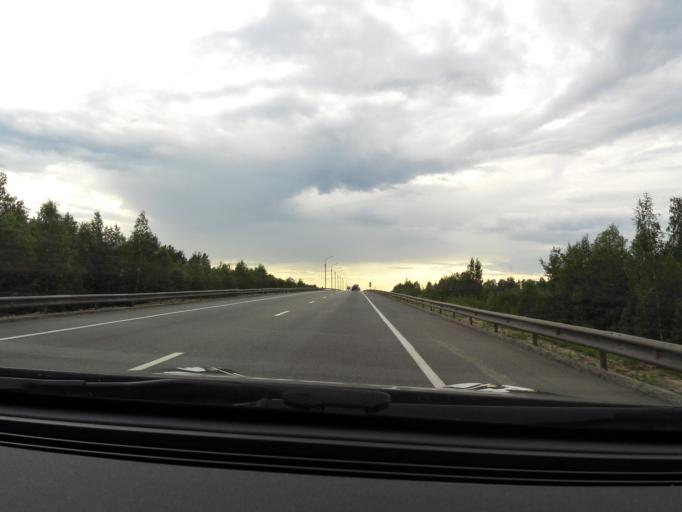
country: RU
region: Vladimir
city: Raduzhnyy
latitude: 56.0735
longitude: 40.2194
